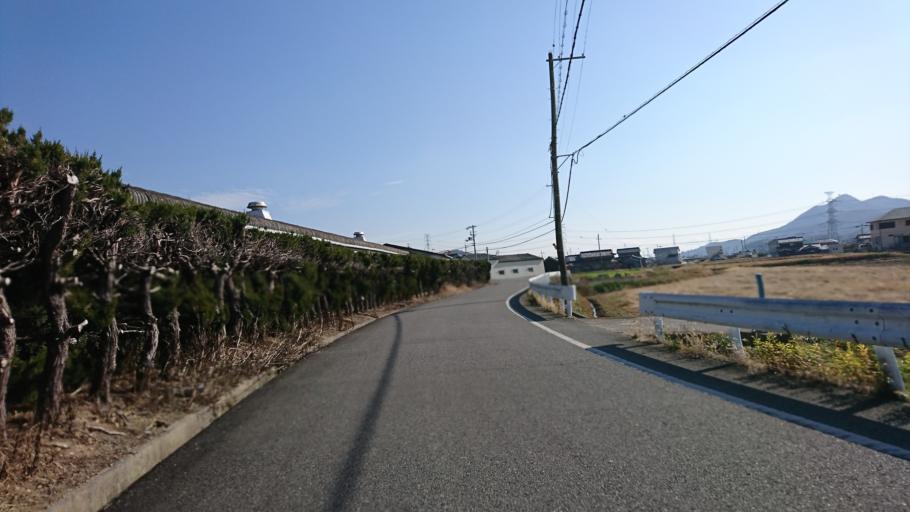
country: JP
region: Hyogo
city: Kakogawacho-honmachi
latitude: 34.8311
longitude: 134.8434
